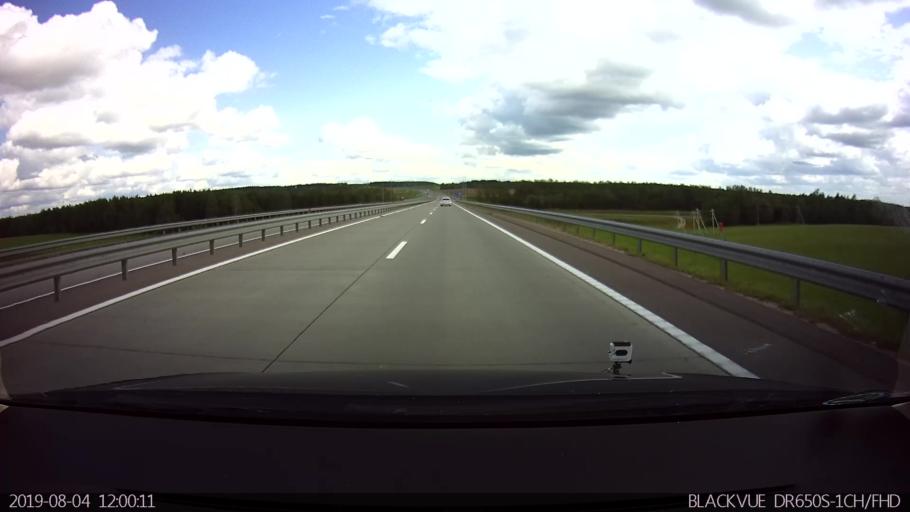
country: BY
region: Minsk
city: Pyatryshki
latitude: 54.0556
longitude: 27.2093
